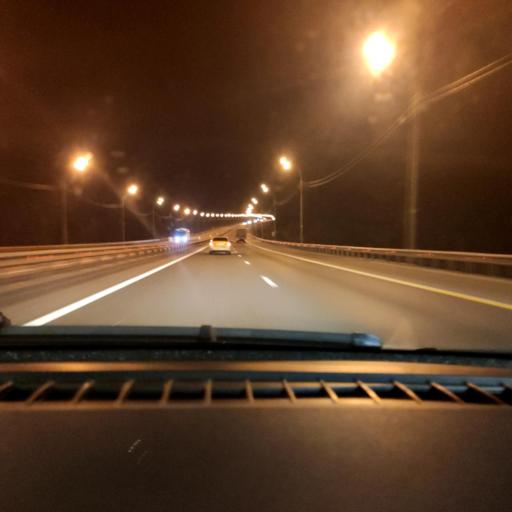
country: RU
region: Lipetsk
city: Khlevnoye
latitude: 52.2245
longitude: 39.1071
